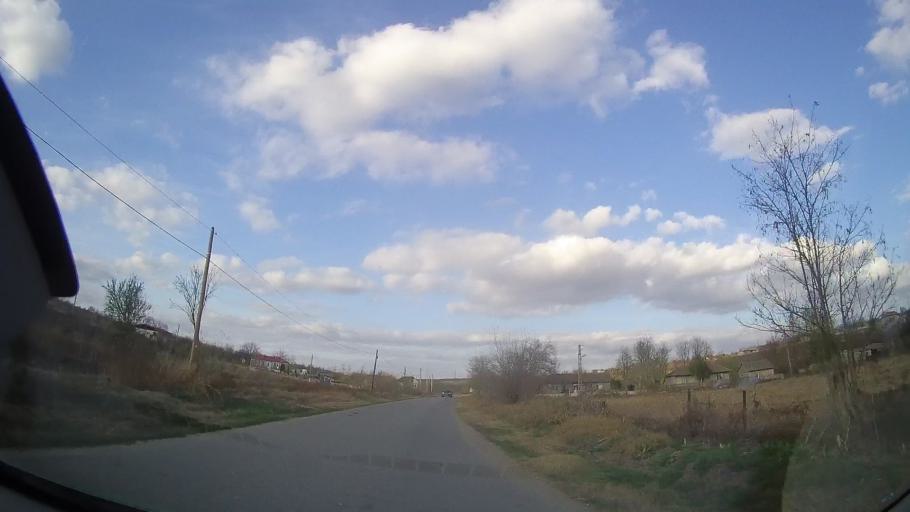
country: RO
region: Constanta
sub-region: Comuna Cerchezu
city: Cerchezu
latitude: 43.8252
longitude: 28.0976
